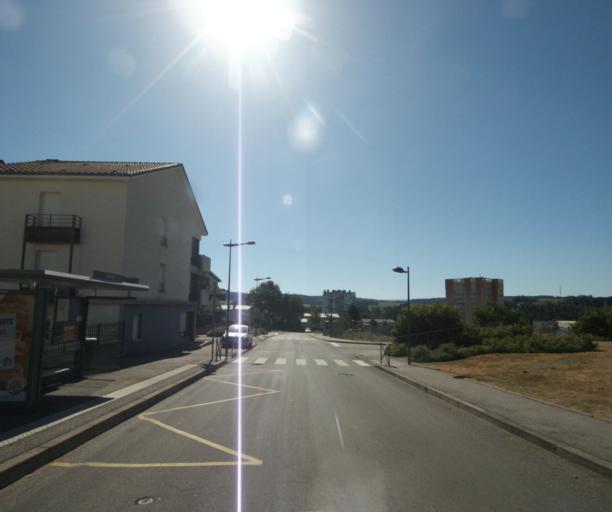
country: FR
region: Lorraine
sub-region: Departement des Vosges
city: Epinal
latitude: 48.1818
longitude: 6.4543
